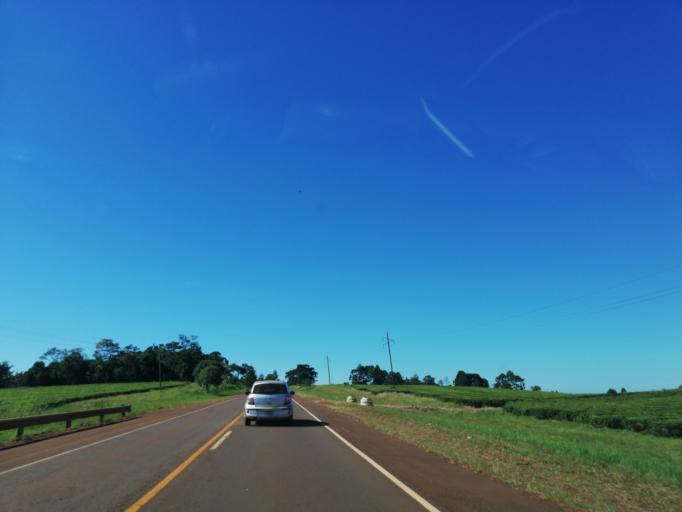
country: AR
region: Misiones
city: Dos de Mayo
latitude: -27.0659
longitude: -54.4186
